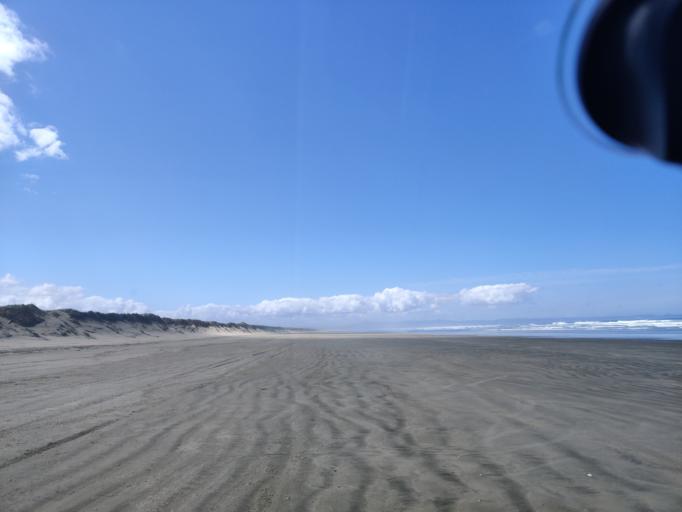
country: NZ
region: Northland
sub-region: Far North District
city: Kaitaia
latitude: -34.9447
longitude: 173.1179
